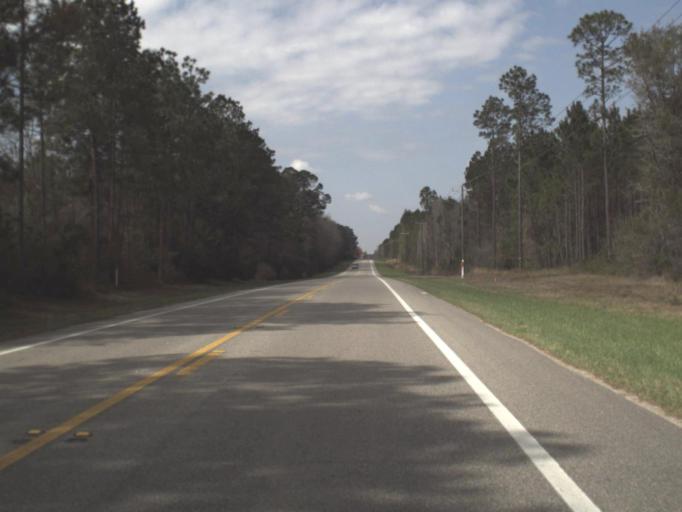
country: US
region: Florida
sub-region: Gadsden County
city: Quincy
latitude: 30.3886
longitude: -84.6972
